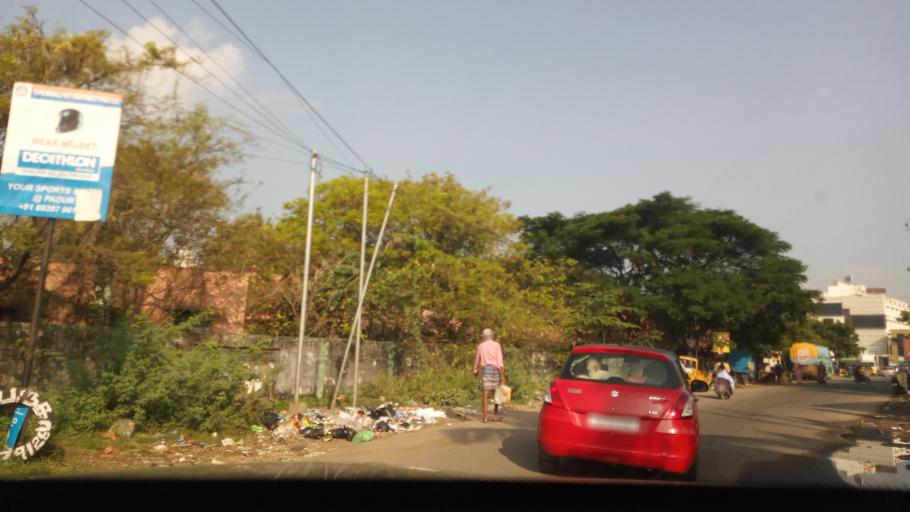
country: IN
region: Tamil Nadu
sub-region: Kancheepuram
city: Vengavasal
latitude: 12.7845
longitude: 80.2214
